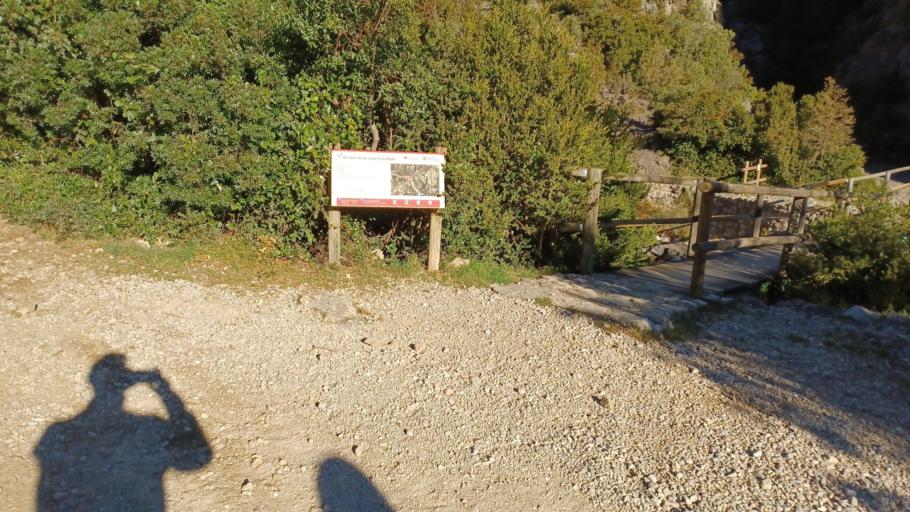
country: ES
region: Catalonia
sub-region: Provincia de Tarragona
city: Mas de Barberans
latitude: 40.7458
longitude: 0.3305
